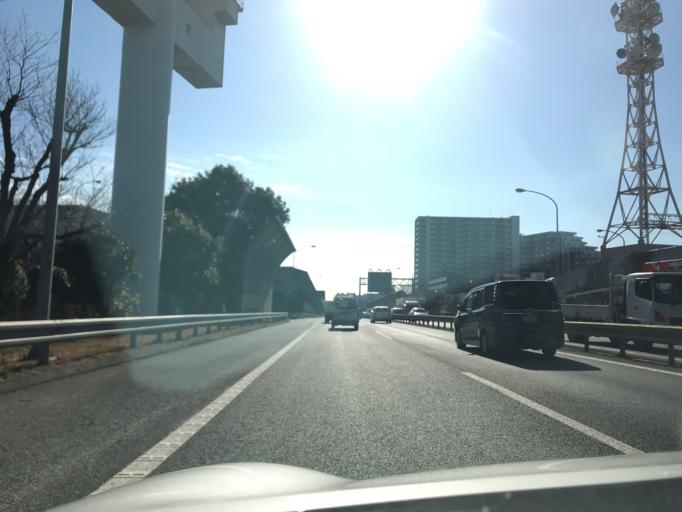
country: JP
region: Chiba
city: Chiba
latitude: 35.6419
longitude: 140.1140
